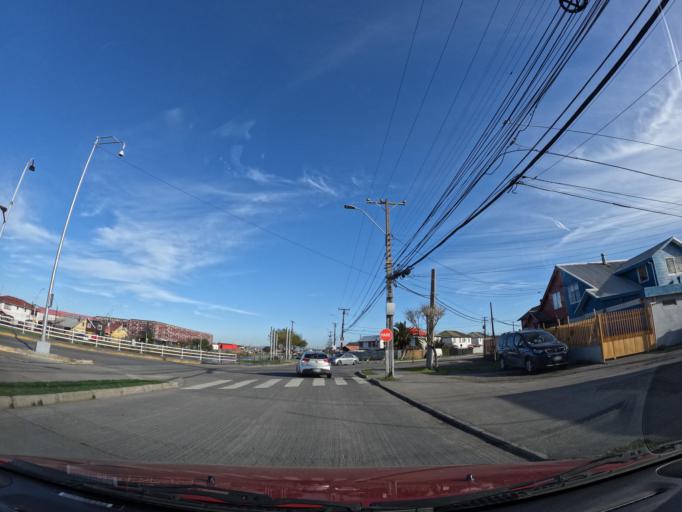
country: CL
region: Biobio
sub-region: Provincia de Concepcion
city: Talcahuano
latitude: -36.7505
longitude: -73.0848
